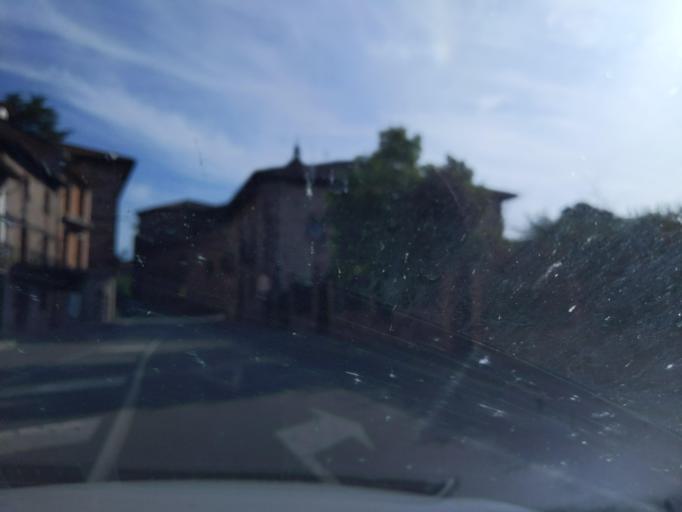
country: ES
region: La Rioja
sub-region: Provincia de La Rioja
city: Ezcaray
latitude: 42.3268
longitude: -3.0140
